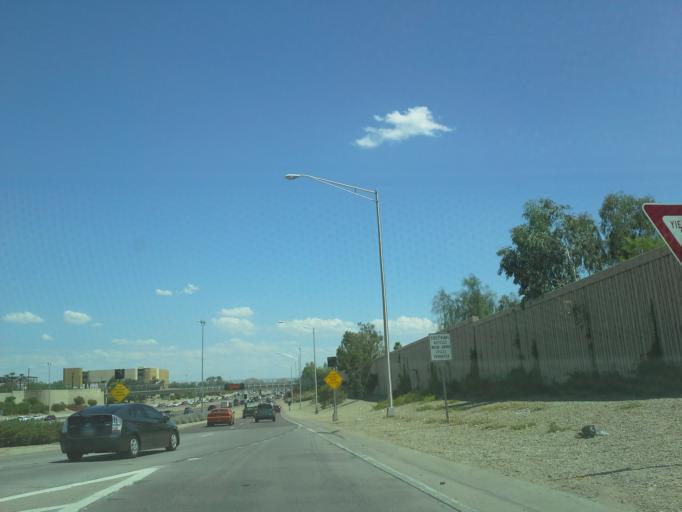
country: US
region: Arizona
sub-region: Maricopa County
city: Phoenix
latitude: 33.4615
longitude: -112.0643
